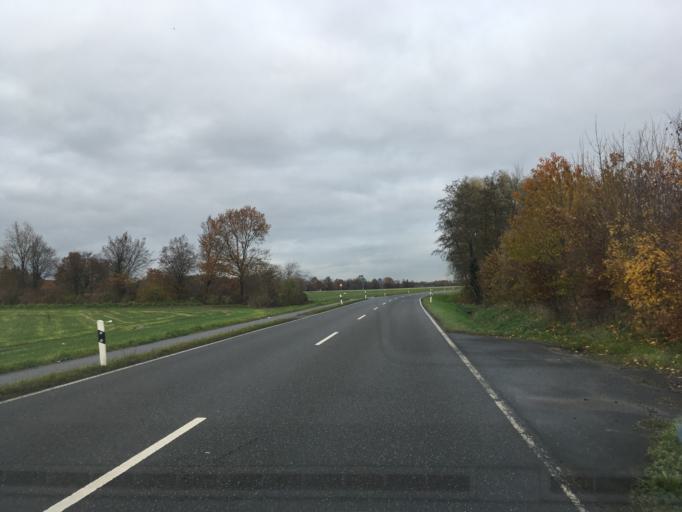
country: DE
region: North Rhine-Westphalia
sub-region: Regierungsbezirk Munster
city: Gescher
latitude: 51.9830
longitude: 7.0269
